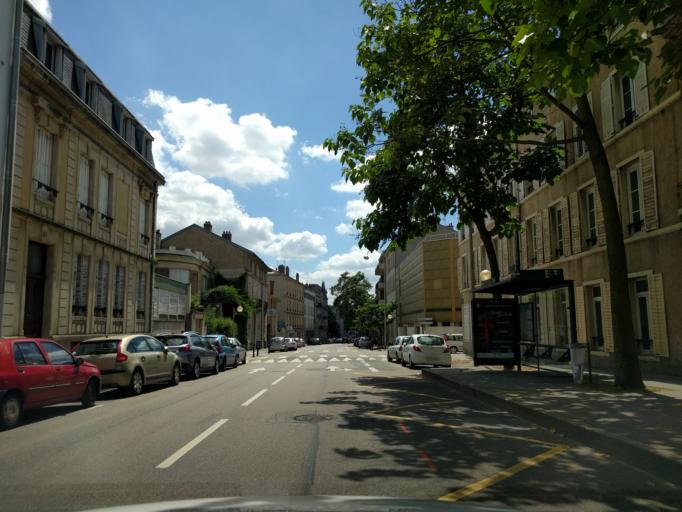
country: FR
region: Lorraine
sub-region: Departement de Meurthe-et-Moselle
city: Laxou
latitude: 48.6877
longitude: 6.1662
